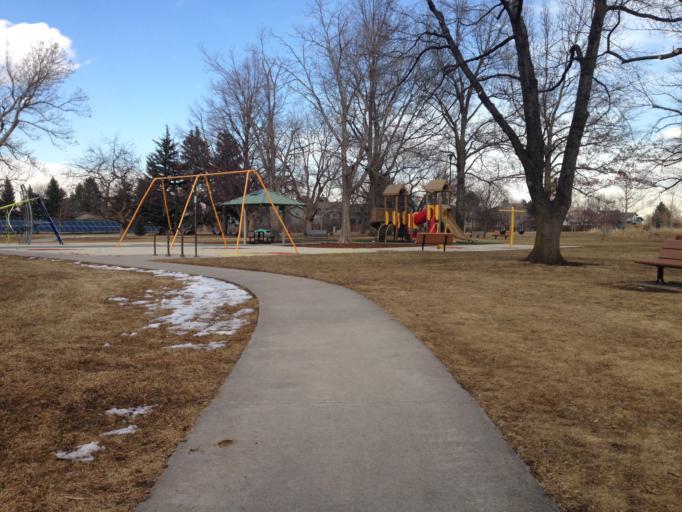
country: US
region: Colorado
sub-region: Boulder County
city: Boulder
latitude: 39.9924
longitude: -105.2280
